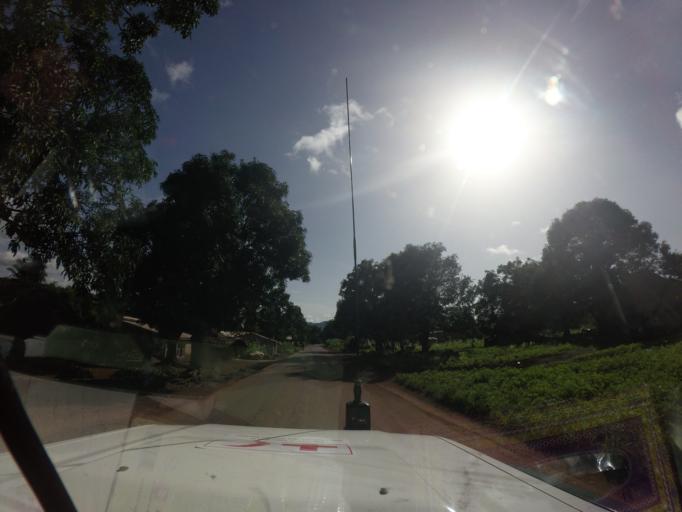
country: GN
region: Mamou
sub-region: Mamou Prefecture
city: Mamou
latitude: 10.2818
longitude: -12.4326
